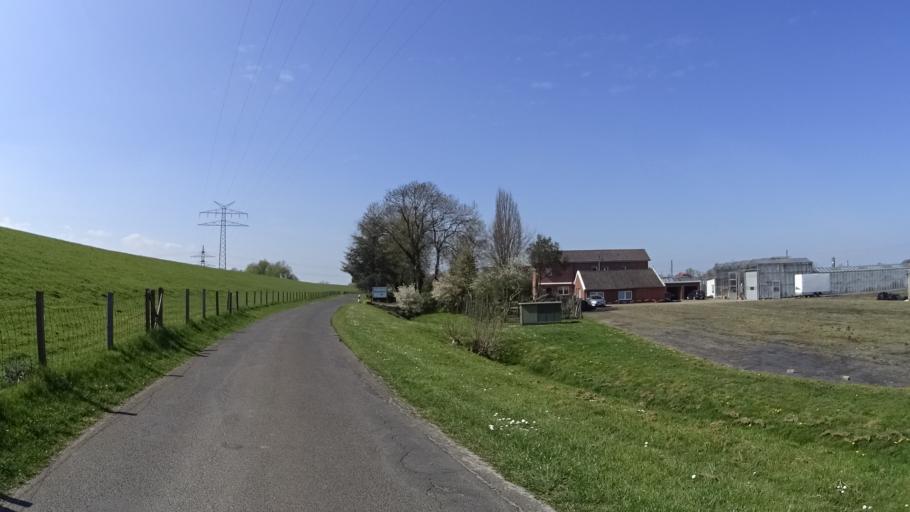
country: DE
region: Lower Saxony
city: Papenburg
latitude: 53.1054
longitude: 7.3578
